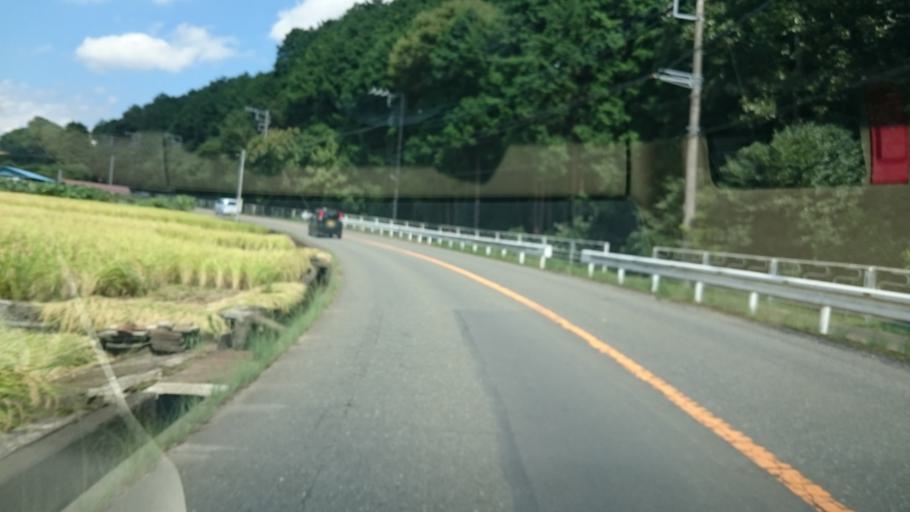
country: JP
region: Shizuoka
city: Mishima
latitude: 35.1994
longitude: 138.9250
